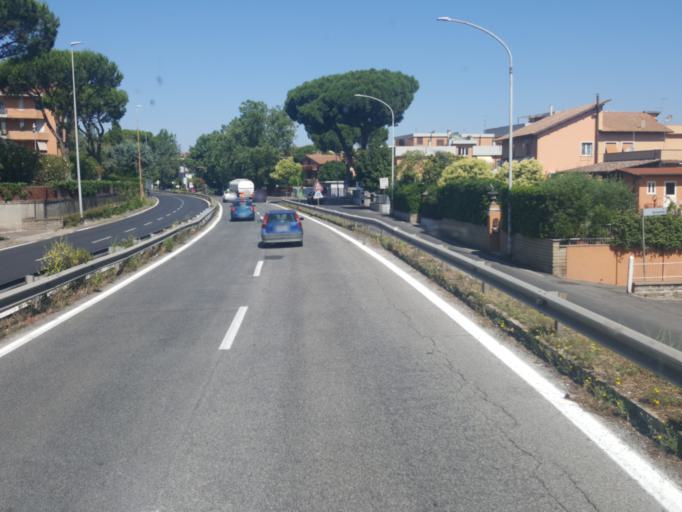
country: IT
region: Latium
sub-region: Citta metropolitana di Roma Capitale
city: Ciampino
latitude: 41.8310
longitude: 12.6192
